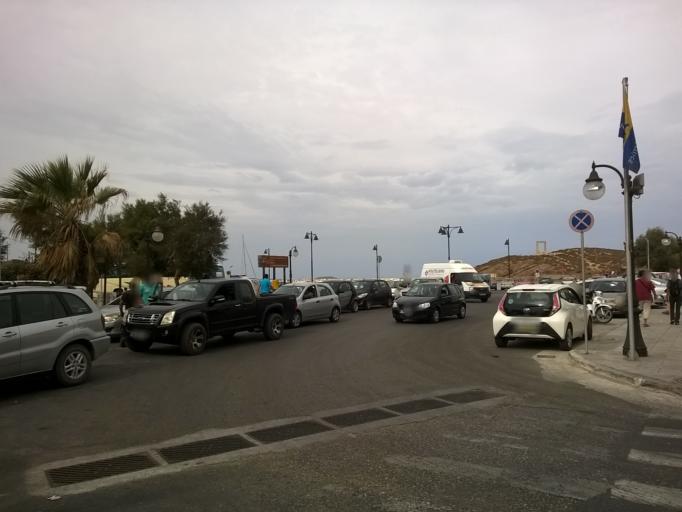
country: GR
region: South Aegean
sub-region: Nomos Kykladon
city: Naxos
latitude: 37.1073
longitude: 25.3746
